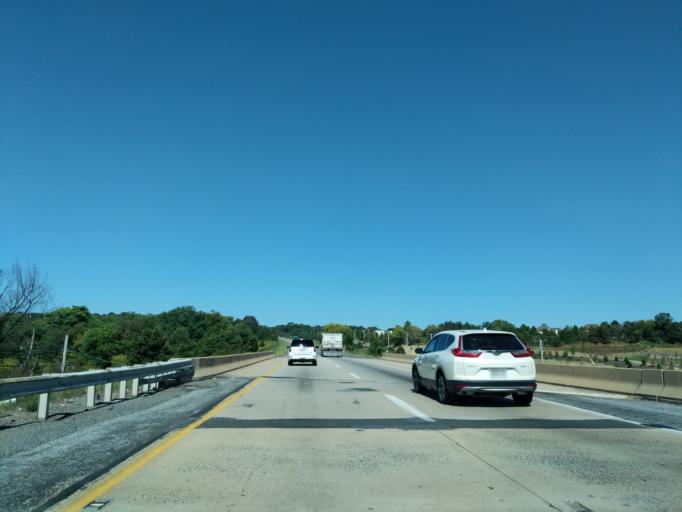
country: US
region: Pennsylvania
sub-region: Montgomery County
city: Audubon
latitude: 40.1419
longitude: -75.4512
